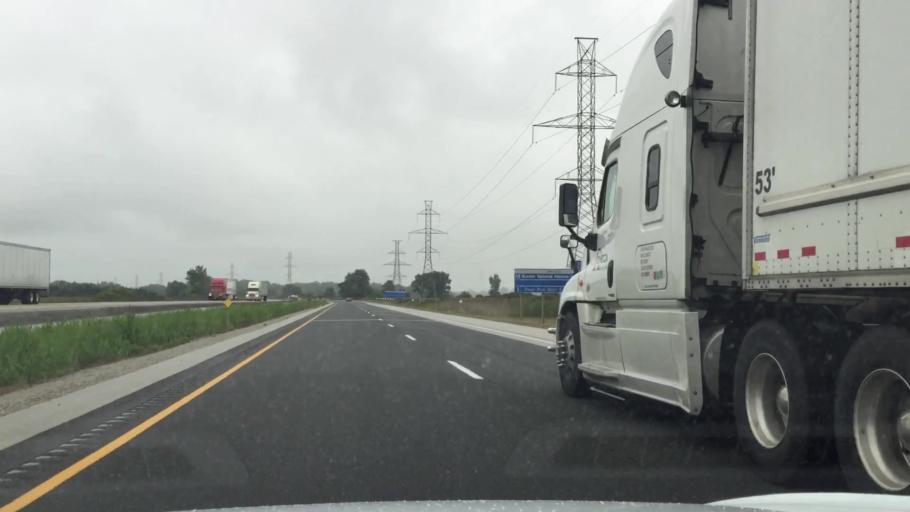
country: CA
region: Ontario
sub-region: Lambton County
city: Walpole Island
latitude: 42.3341
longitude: -82.2117
